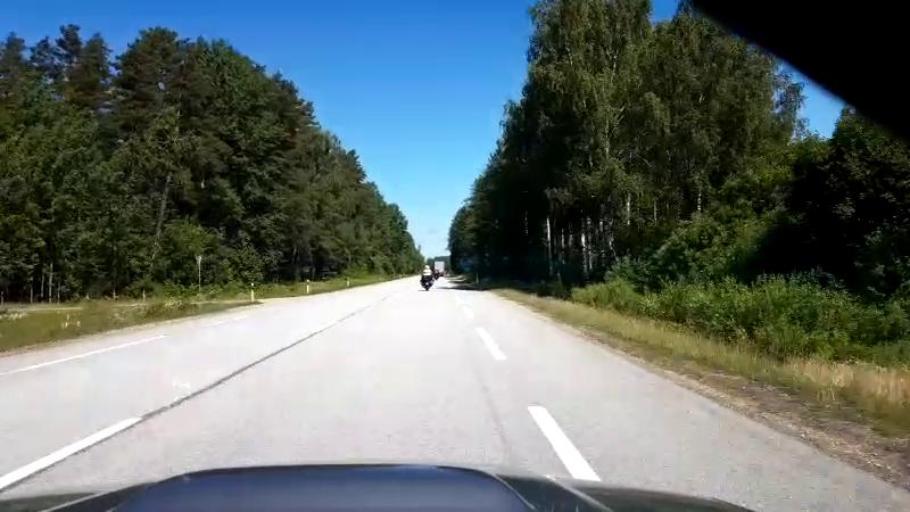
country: LV
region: Saulkrastu
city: Saulkrasti
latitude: 57.4299
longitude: 24.4295
